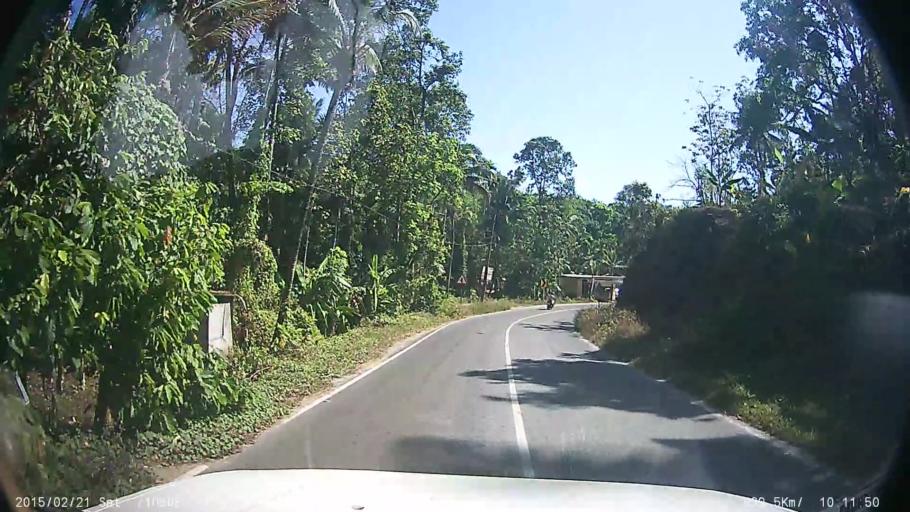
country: IN
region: Kerala
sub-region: Ernakulam
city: Muvattupuzha
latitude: 9.8871
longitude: 76.6195
